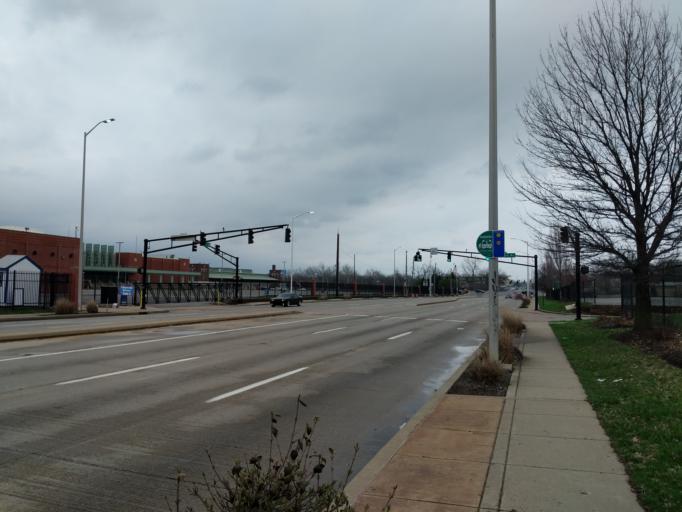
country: US
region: Indiana
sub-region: Marion County
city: Broad Ripple
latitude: 39.8253
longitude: -86.1352
